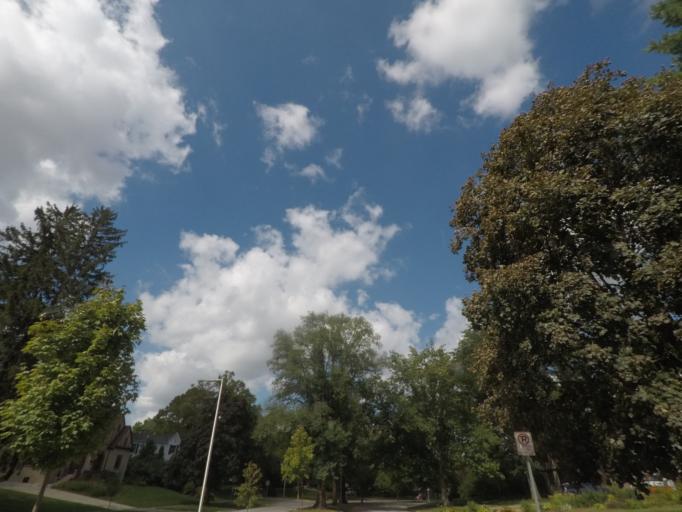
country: US
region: Iowa
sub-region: Story County
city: Ames
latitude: 42.0163
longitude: -93.6425
